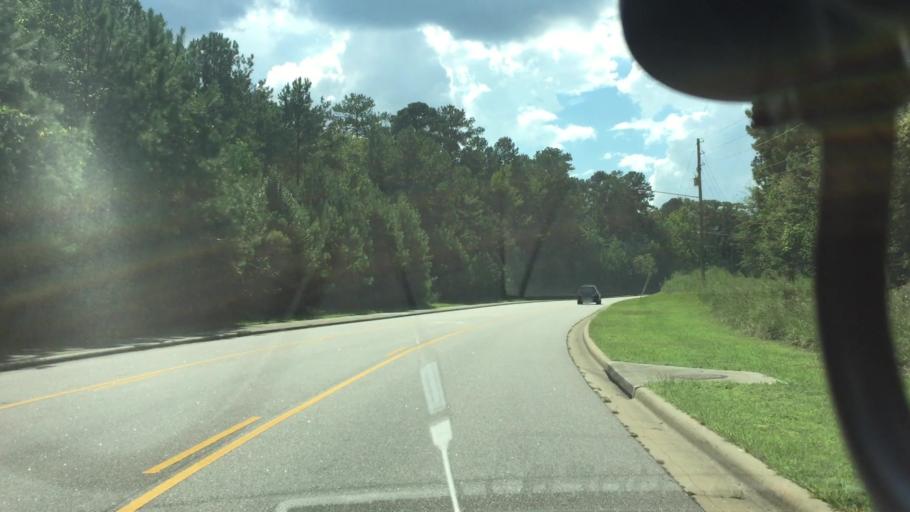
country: US
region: Alabama
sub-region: Lee County
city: Auburn
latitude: 32.5688
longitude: -85.5183
